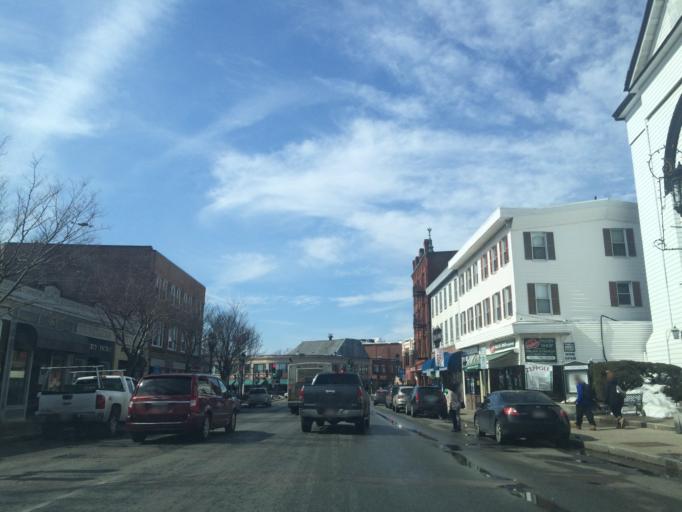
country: US
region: Massachusetts
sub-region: Middlesex County
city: Medford
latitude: 42.4186
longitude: -71.1084
